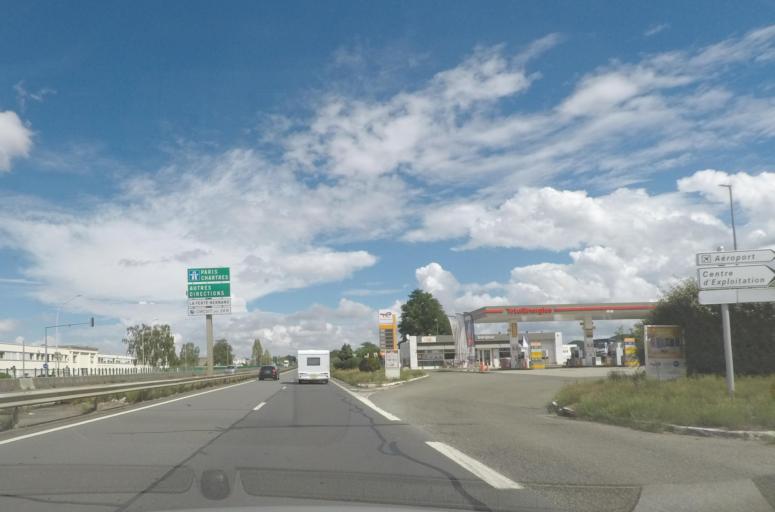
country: FR
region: Pays de la Loire
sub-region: Departement de la Sarthe
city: Arnage
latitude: 47.9480
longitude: 0.1945
